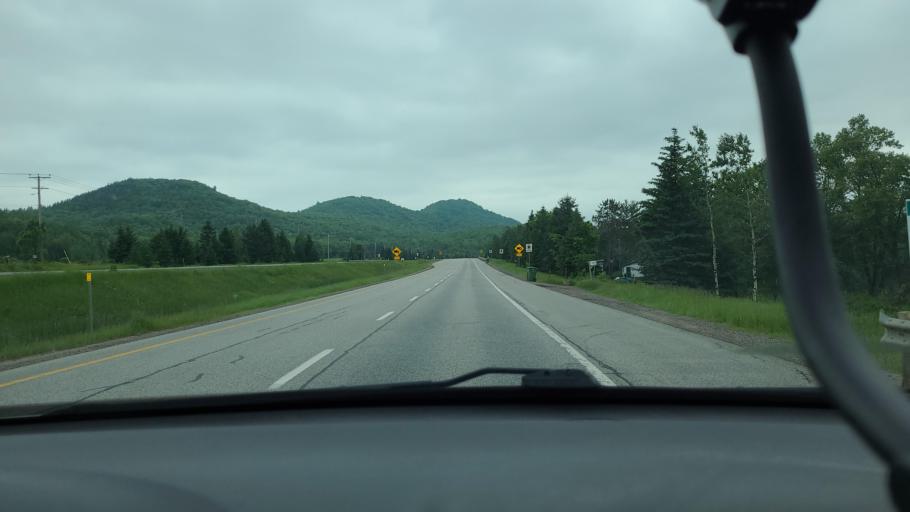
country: CA
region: Quebec
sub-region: Laurentides
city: Labelle
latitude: 46.1876
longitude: -74.7303
